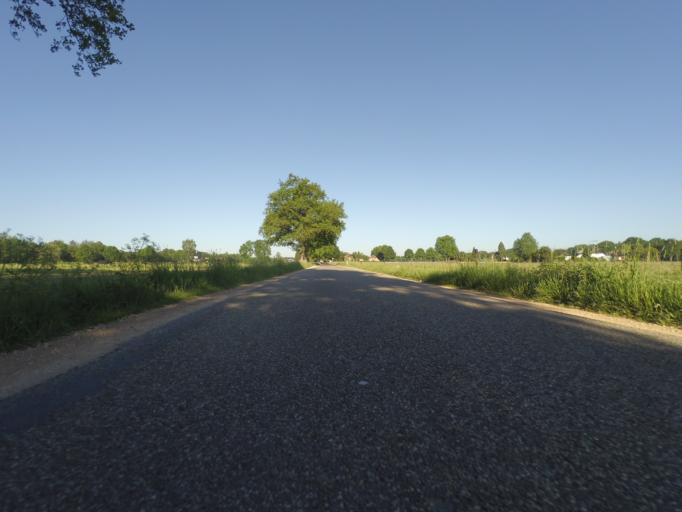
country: NL
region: Gelderland
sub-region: Gemeente Apeldoorn
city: Beekbergen
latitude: 52.1696
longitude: 5.9845
